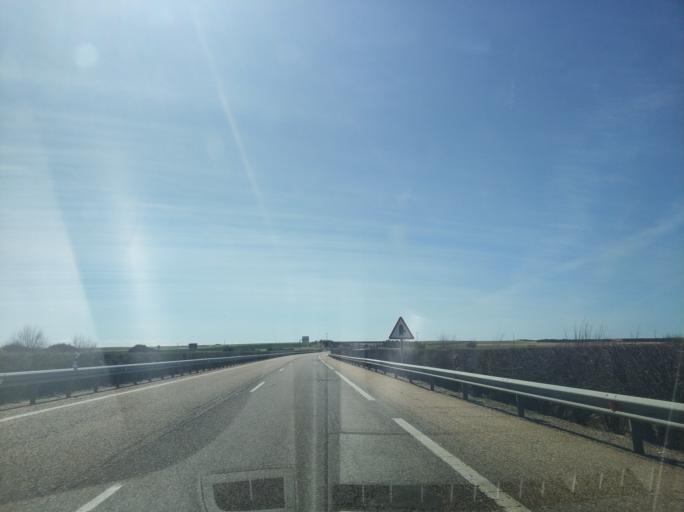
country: ES
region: Castille and Leon
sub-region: Provincia de Valladolid
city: Alaejos
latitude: 41.3018
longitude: -5.2301
